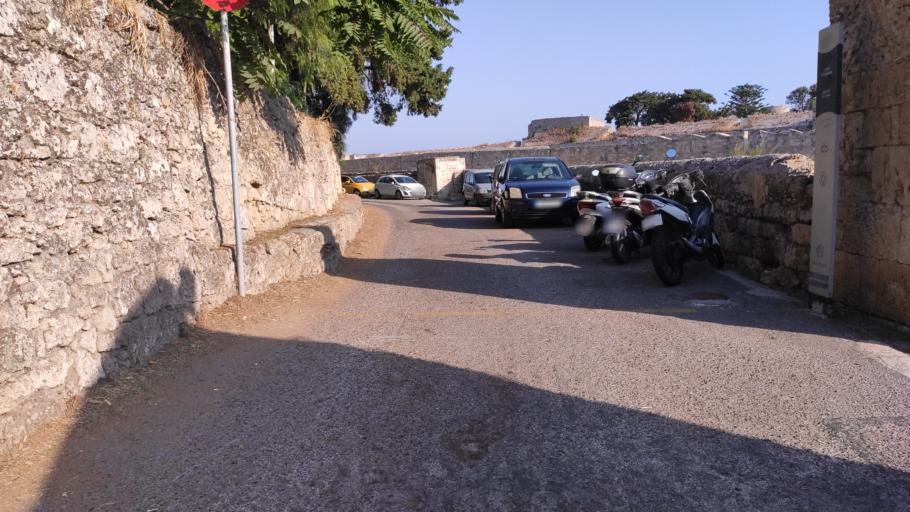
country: GR
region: South Aegean
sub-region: Nomos Dodekanisou
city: Rodos
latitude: 36.4394
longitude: 28.2277
